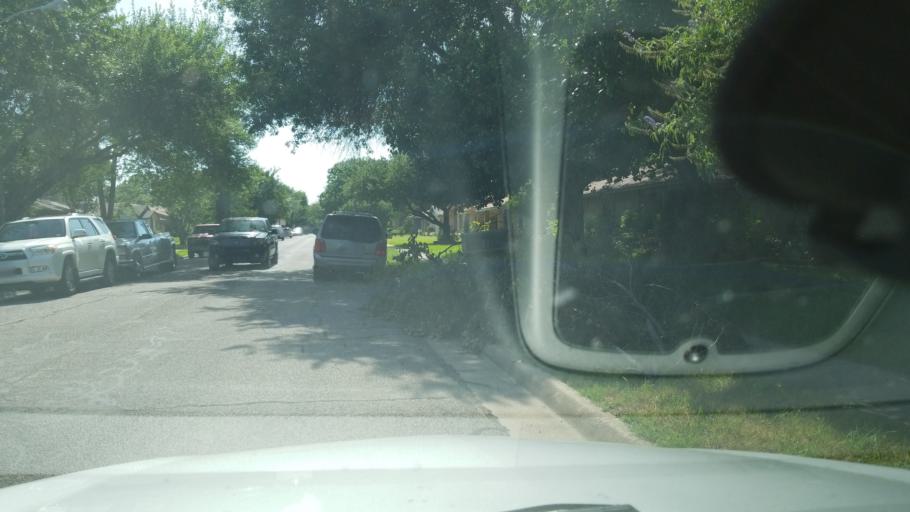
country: US
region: Texas
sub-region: Dallas County
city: Irving
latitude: 32.8141
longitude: -96.9743
